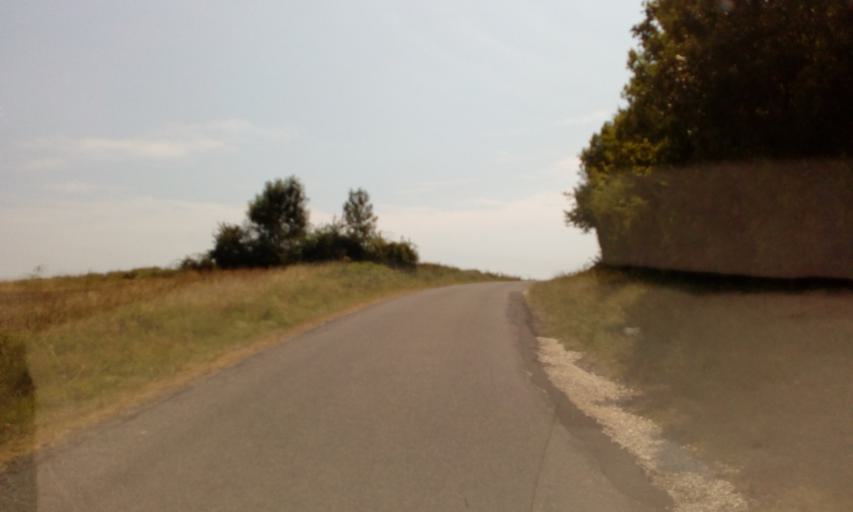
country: FR
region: Lorraine
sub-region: Departement de la Meuse
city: Verdun
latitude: 49.2339
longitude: 5.4755
